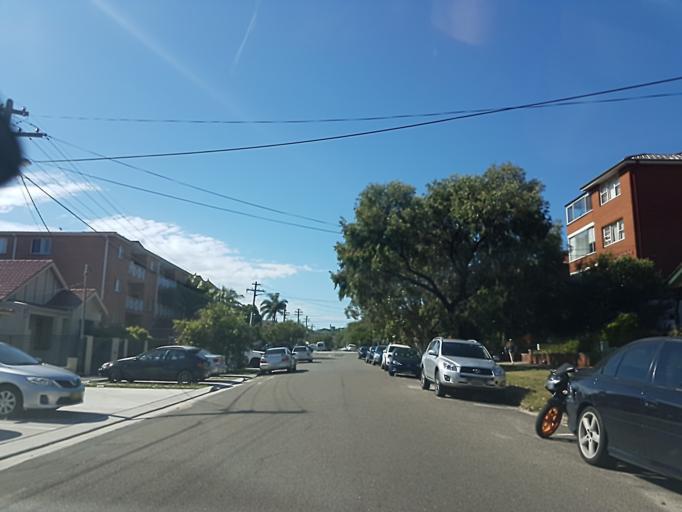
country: AU
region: New South Wales
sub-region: Randwick
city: Kingsford
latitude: -33.9237
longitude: 151.2296
